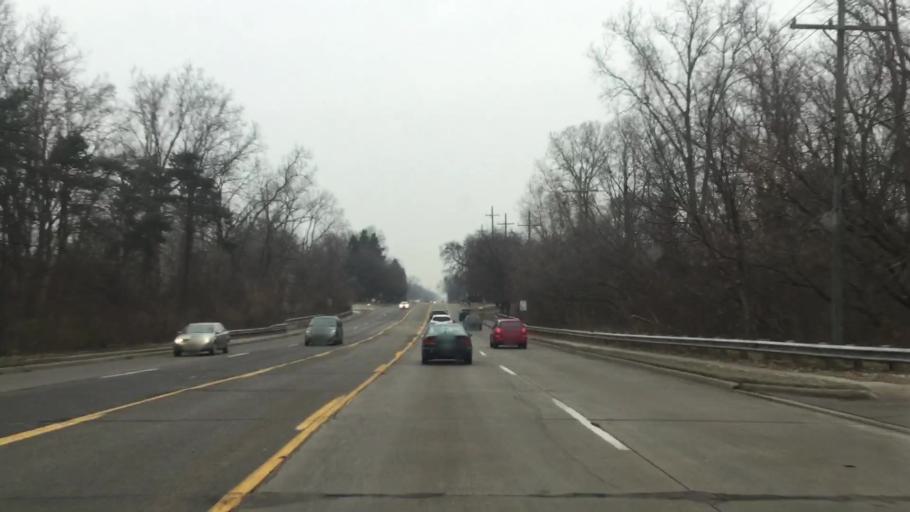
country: US
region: Michigan
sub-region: Oakland County
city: Farmington
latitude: 42.4197
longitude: -83.3550
